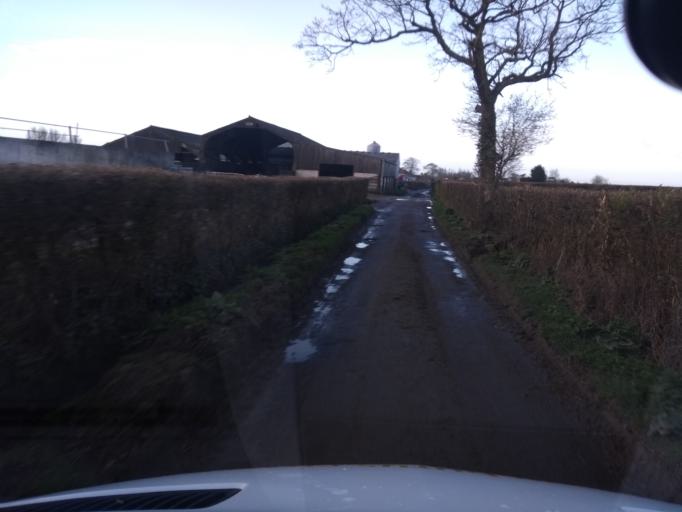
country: GB
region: England
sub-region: Somerset
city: Wedmore
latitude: 51.2291
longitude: -2.8382
